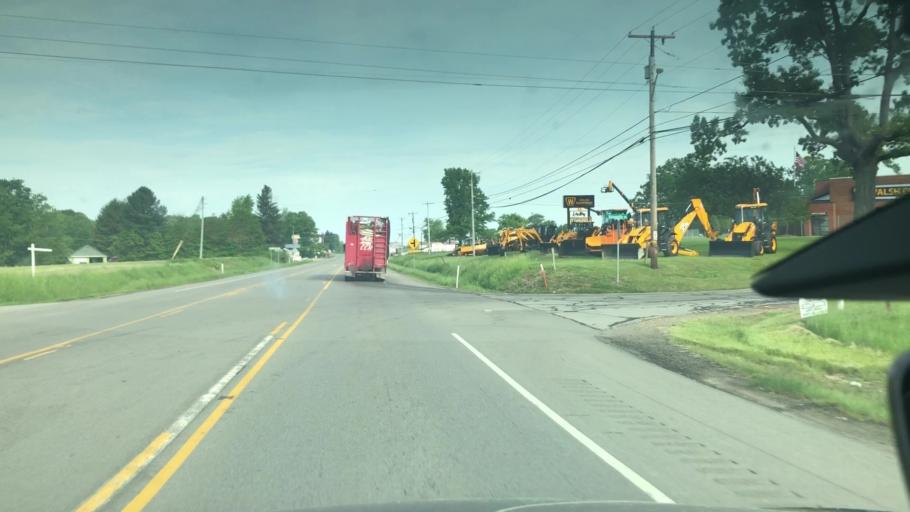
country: US
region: Pennsylvania
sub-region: Butler County
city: Prospect
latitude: 40.9087
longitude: -80.0315
